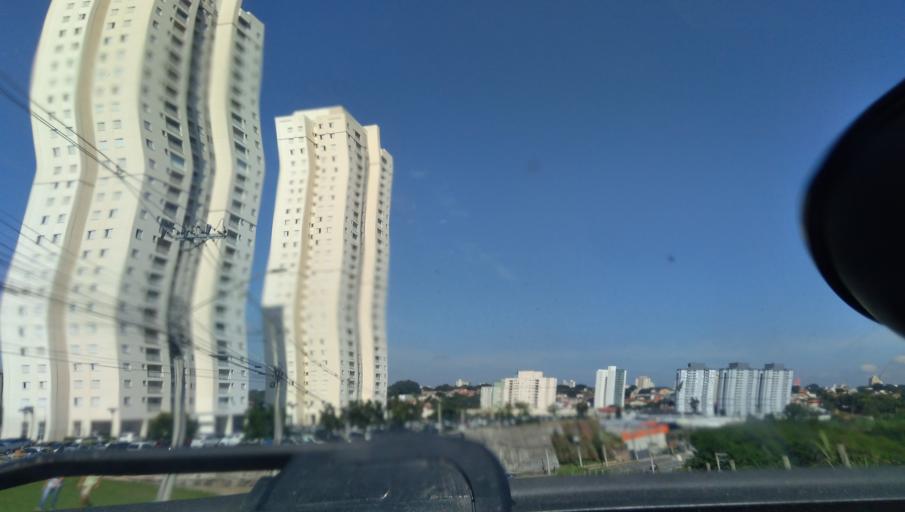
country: BR
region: Sao Paulo
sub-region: Sao Jose Dos Campos
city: Sao Jose dos Campos
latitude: -23.1787
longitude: -45.8634
